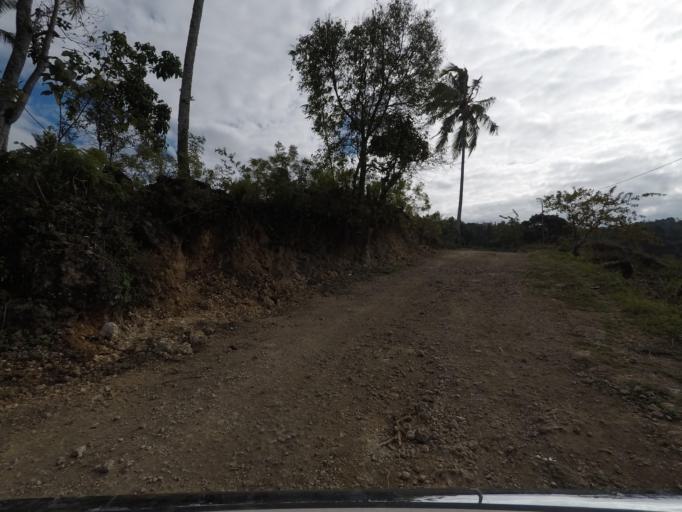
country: TL
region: Baucau
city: Venilale
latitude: -8.6479
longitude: 126.3924
